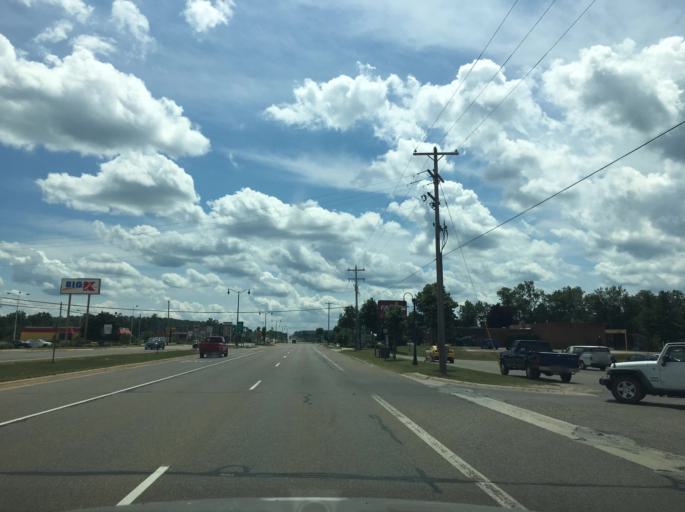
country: US
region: Michigan
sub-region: Crawford County
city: Grayling
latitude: 44.6508
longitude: -84.7087
